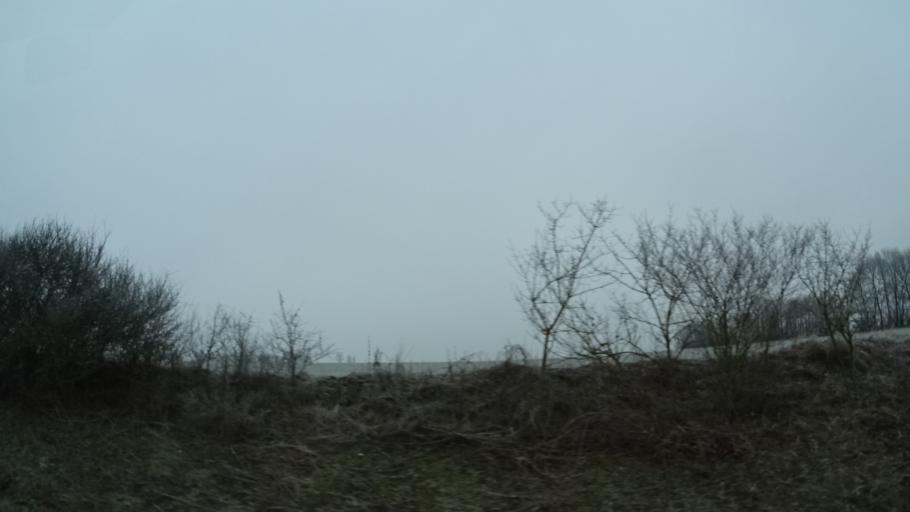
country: DE
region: Bavaria
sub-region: Regierungsbezirk Unterfranken
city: Burgpreppach
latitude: 50.1310
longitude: 10.6272
